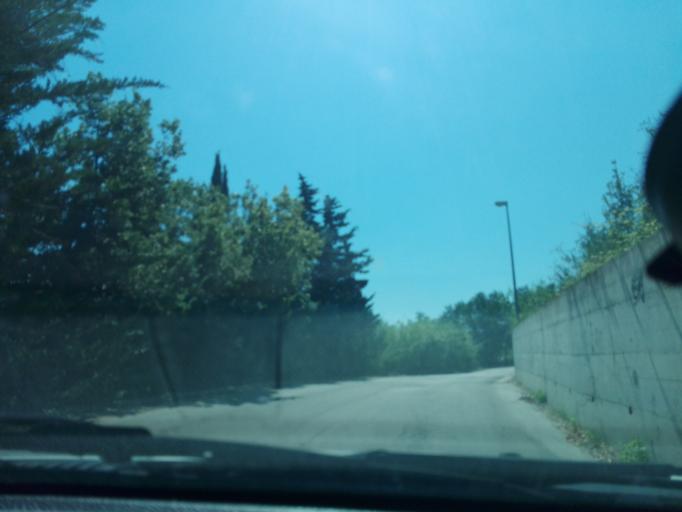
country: IT
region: Abruzzo
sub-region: Provincia di Pescara
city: Montesilvano Marina
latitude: 42.4996
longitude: 14.1588
